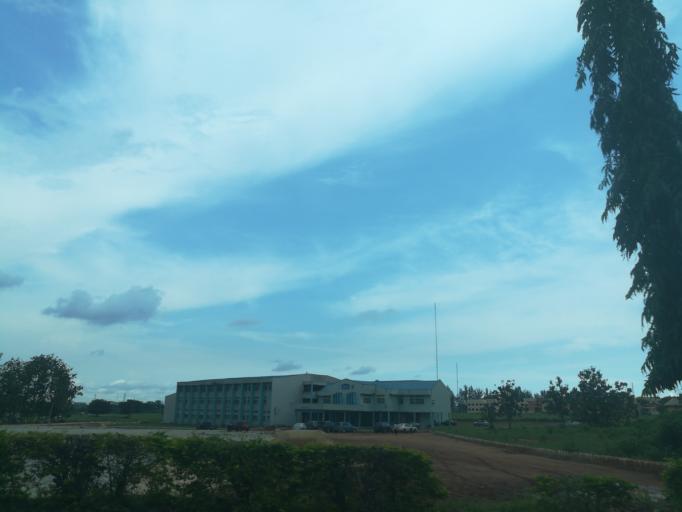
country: NG
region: Lagos
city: Ikorodu
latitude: 6.6419
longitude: 3.5233
